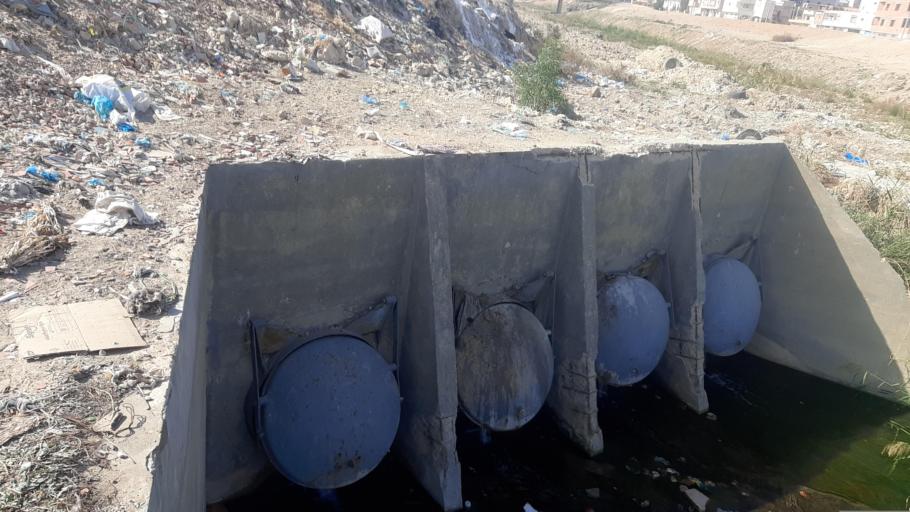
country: TN
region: Qabis
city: Gabes
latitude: 33.8730
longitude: 10.0973
